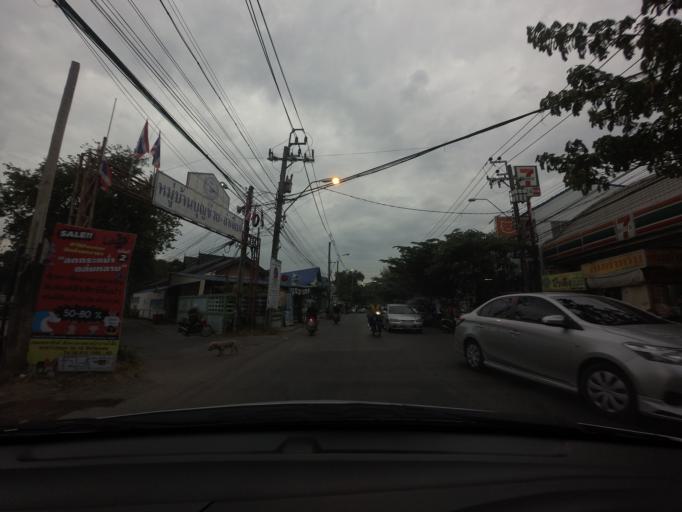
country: TH
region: Bangkok
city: Yan Nawa
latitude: 13.6817
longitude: 100.5660
